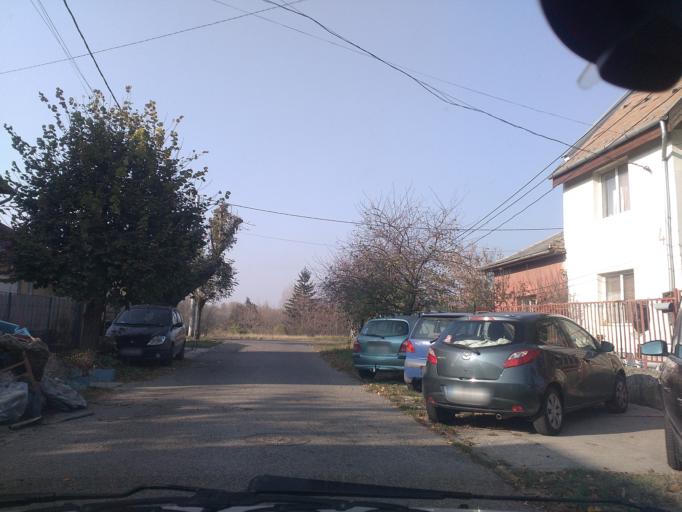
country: HU
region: Budapest
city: Budapest XVIII. keruelet
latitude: 47.4415
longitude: 19.1963
